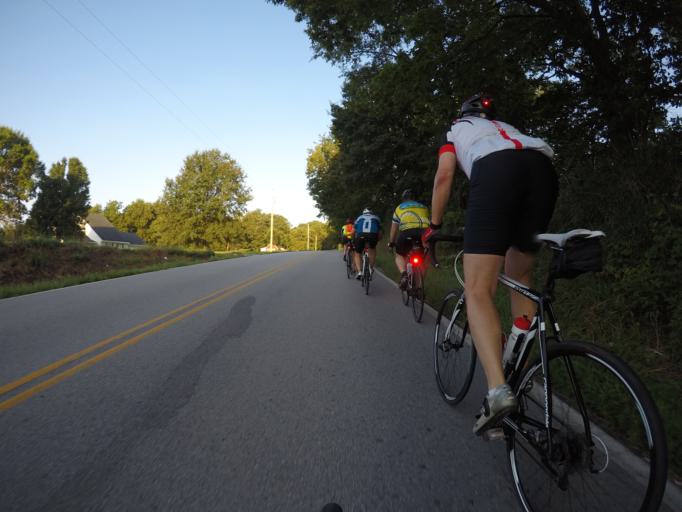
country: US
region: Kansas
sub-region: Leavenworth County
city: Lansing
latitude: 39.2160
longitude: -94.8517
